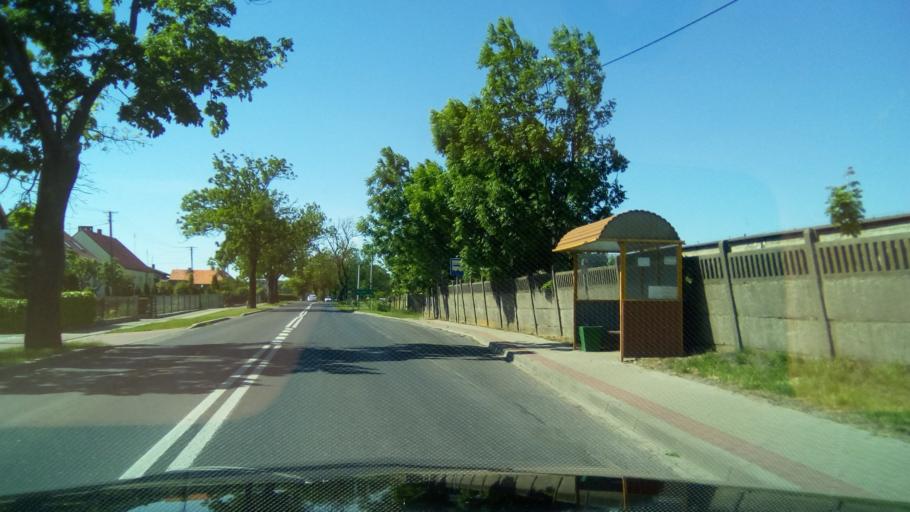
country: PL
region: Greater Poland Voivodeship
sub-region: Powiat gnieznienski
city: Niechanowo
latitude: 52.4824
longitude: 17.6609
